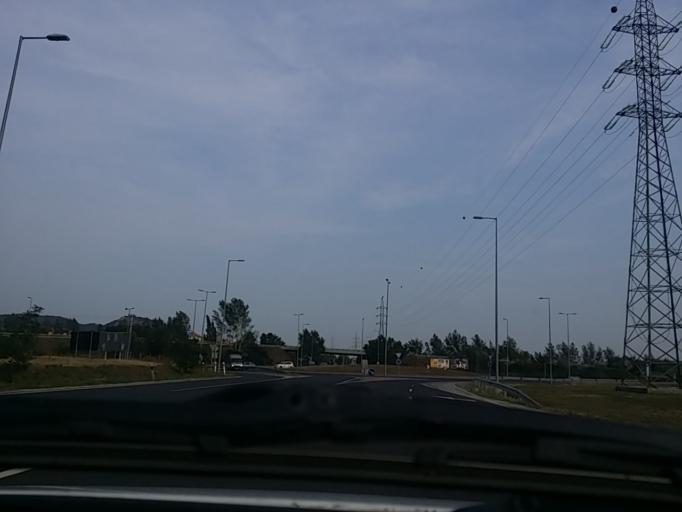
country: HU
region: Pest
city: Toeroekbalint
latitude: 47.4668
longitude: 18.8781
